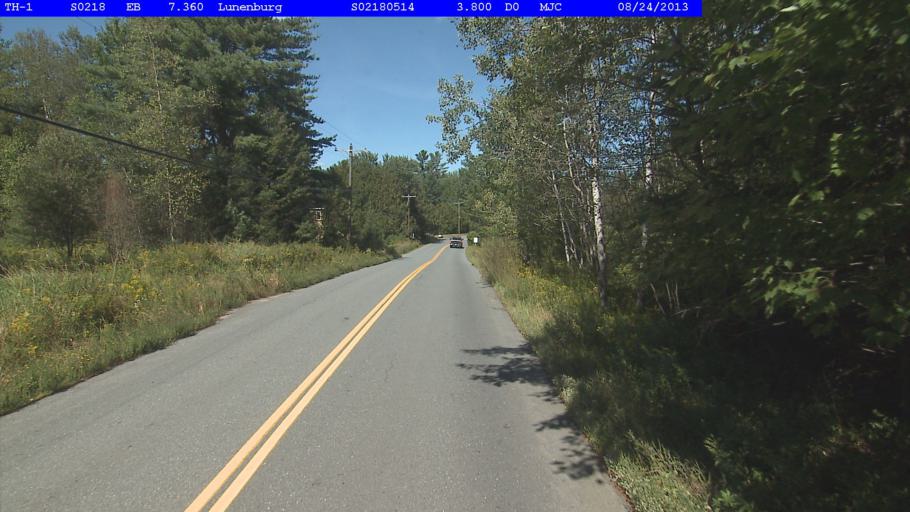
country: US
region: New Hampshire
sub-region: Coos County
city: Whitefield
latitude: 44.4268
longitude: -71.6847
